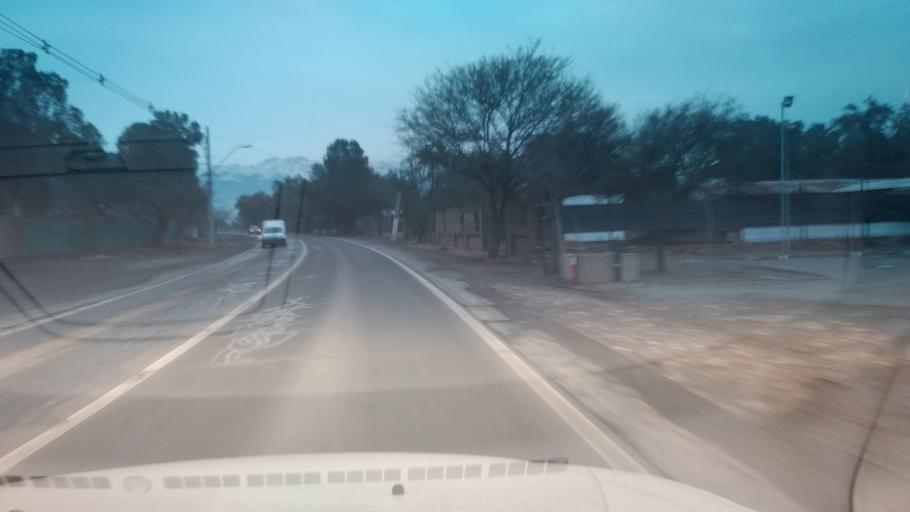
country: CL
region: Santiago Metropolitan
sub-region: Provincia de Chacabuco
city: Chicureo Abajo
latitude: -33.0923
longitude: -70.7313
